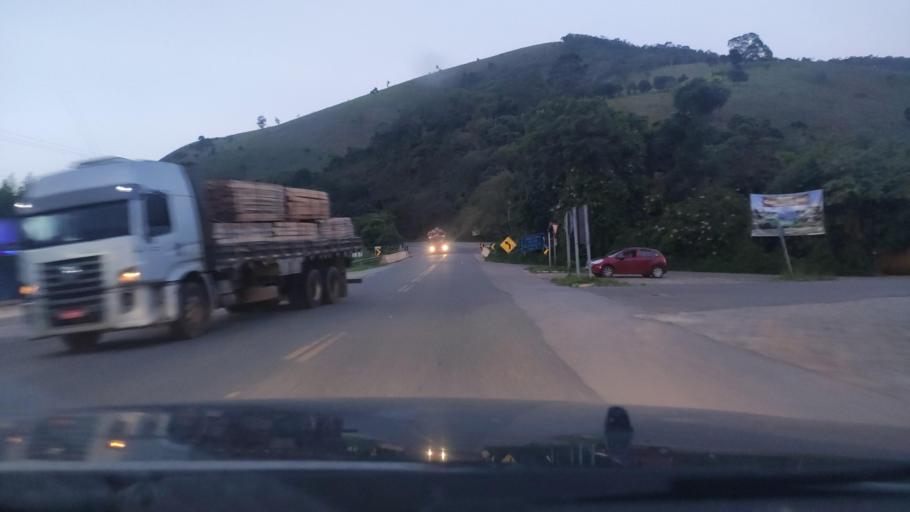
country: BR
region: Sao Paulo
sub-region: Campos Do Jordao
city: Campos do Jordao
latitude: -22.7437
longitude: -45.7394
